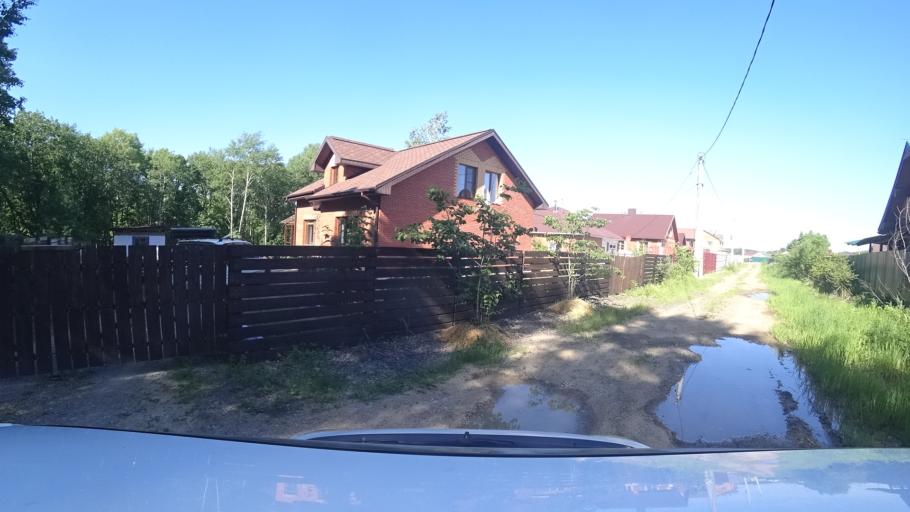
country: RU
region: Khabarovsk Krai
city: Topolevo
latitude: 48.5501
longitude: 135.1806
